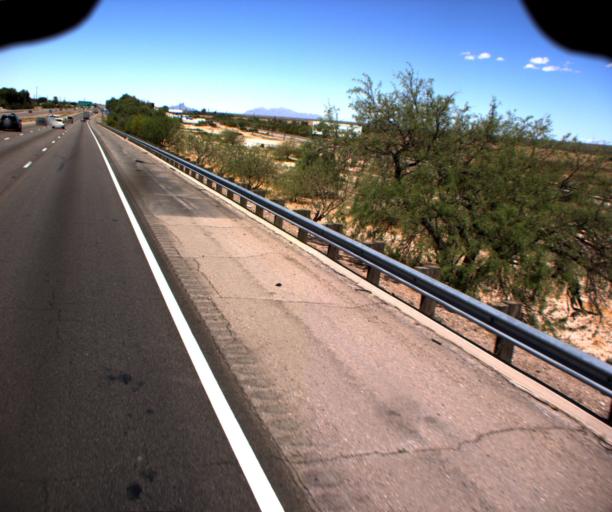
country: US
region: Arizona
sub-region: Pima County
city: Marana
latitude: 32.4100
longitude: -111.1435
